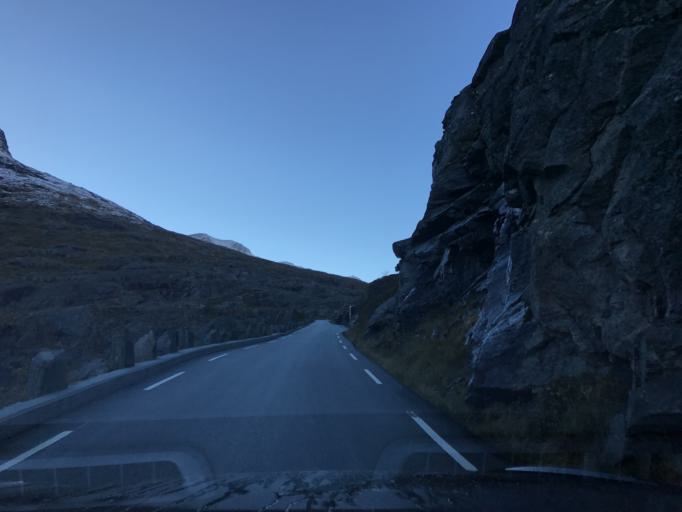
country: NO
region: More og Romsdal
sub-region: Rauma
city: Andalsnes
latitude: 62.4580
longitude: 7.6669
